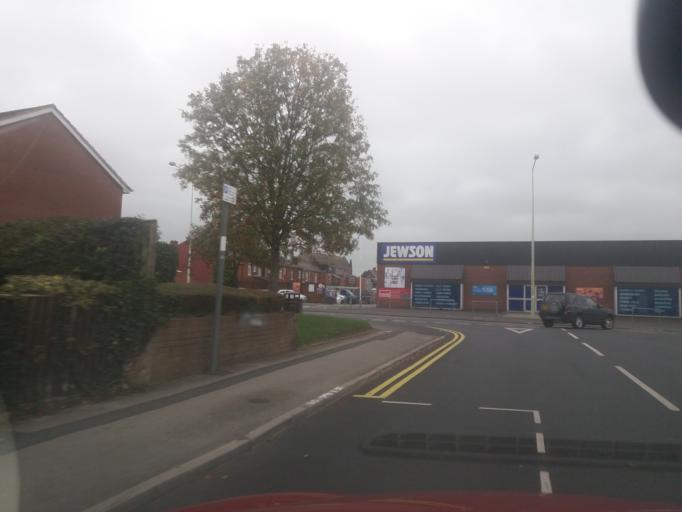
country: GB
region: England
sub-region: Lancashire
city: Chorley
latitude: 53.6515
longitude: -2.6235
